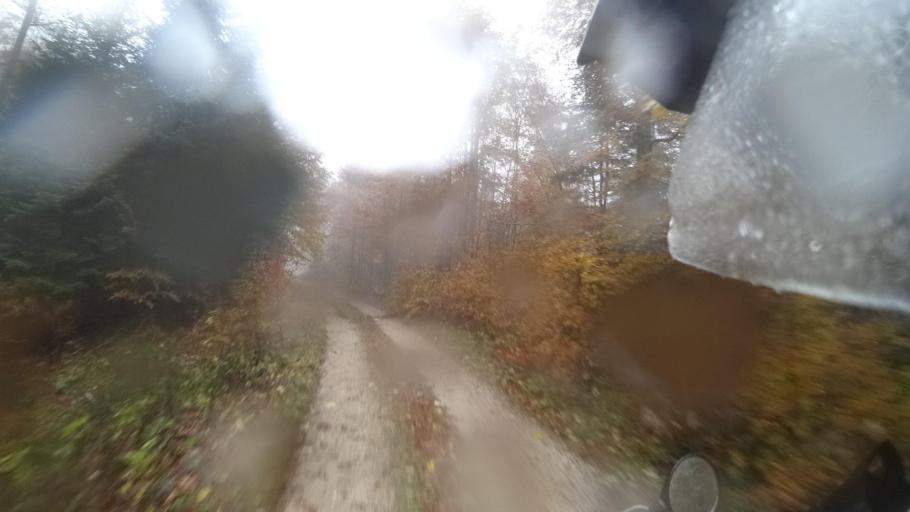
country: HR
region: Primorsko-Goranska
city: Vrbovsko
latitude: 45.2937
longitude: 14.9405
